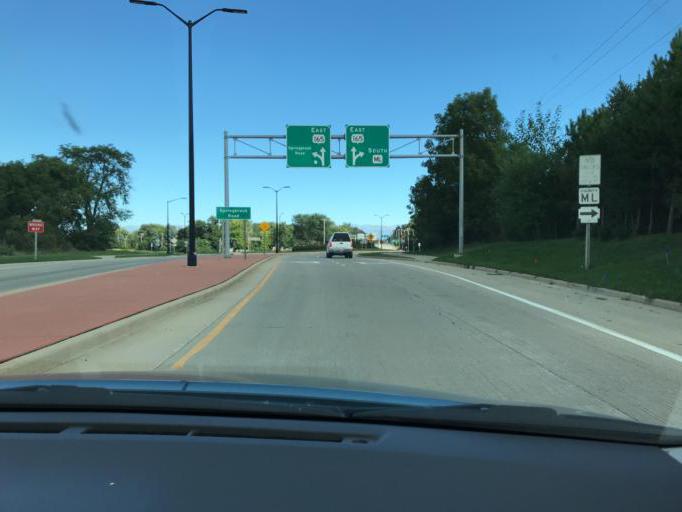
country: US
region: Illinois
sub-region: Lake County
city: Winthrop Harbor
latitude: 42.5225
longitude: -87.8622
